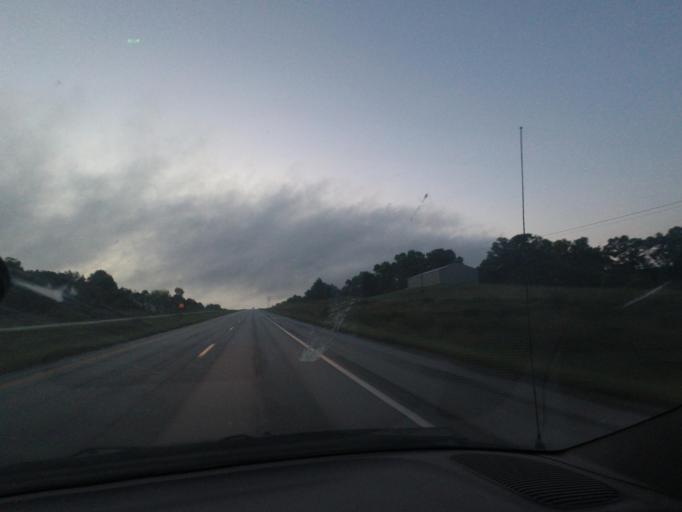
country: US
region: Missouri
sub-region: Linn County
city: Brookfield
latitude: 39.7635
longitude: -93.0319
